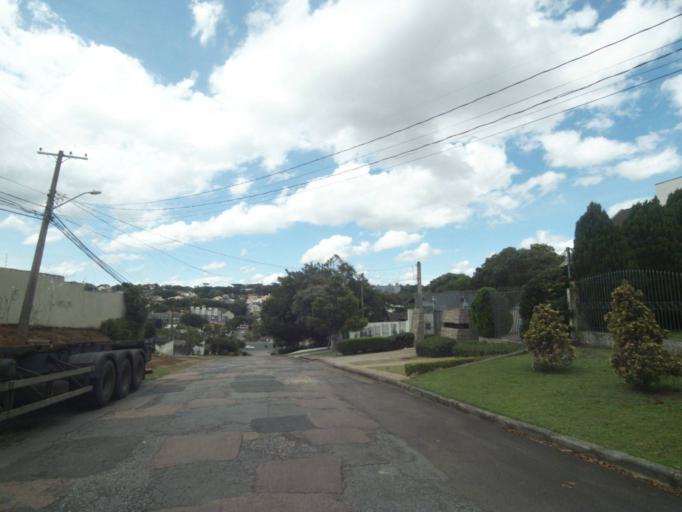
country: BR
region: Parana
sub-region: Curitiba
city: Curitiba
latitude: -25.4320
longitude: -49.3202
